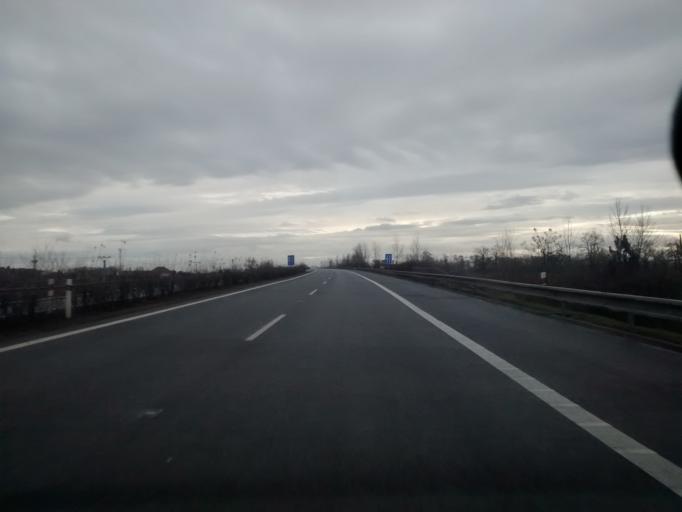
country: CZ
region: Central Bohemia
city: Velvary
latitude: 50.3419
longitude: 14.2804
